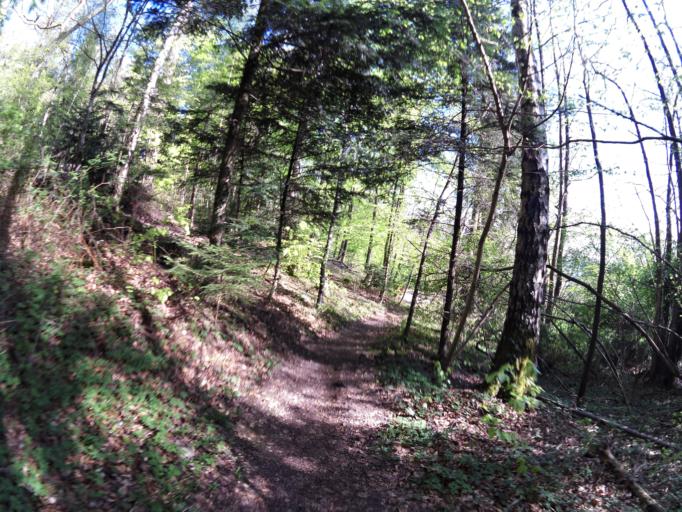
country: CH
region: Solothurn
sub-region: Bezirk Goesgen
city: Niedererlinsbach
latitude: 47.3991
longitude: 8.0238
